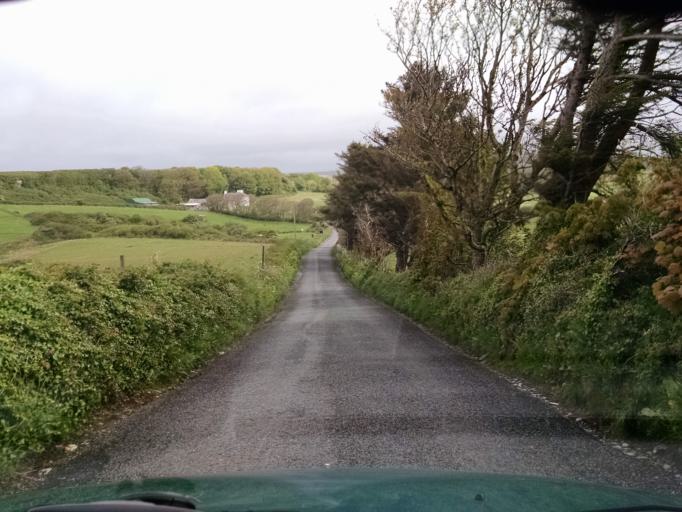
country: IE
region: Connaught
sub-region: County Galway
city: Bearna
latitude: 53.0407
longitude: -9.3473
